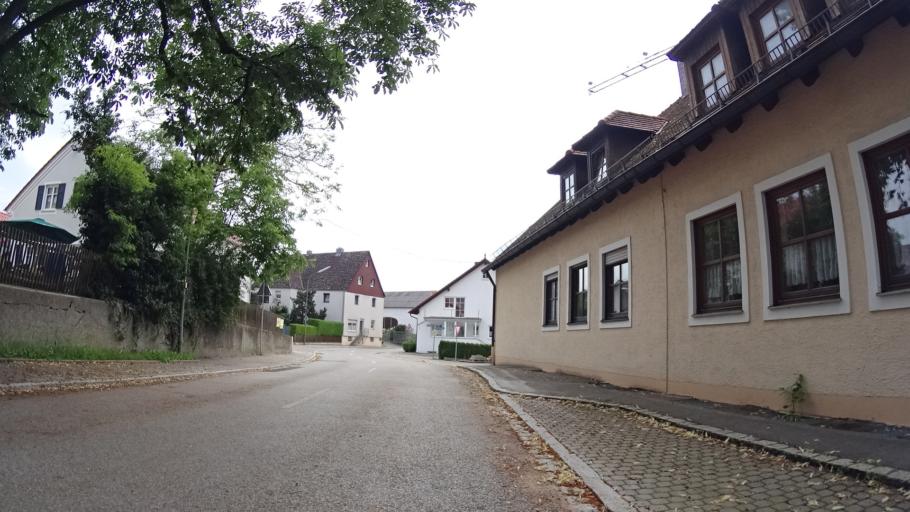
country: DE
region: Bavaria
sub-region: Upper Bavaria
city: Stammham
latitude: 48.8582
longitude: 11.4591
